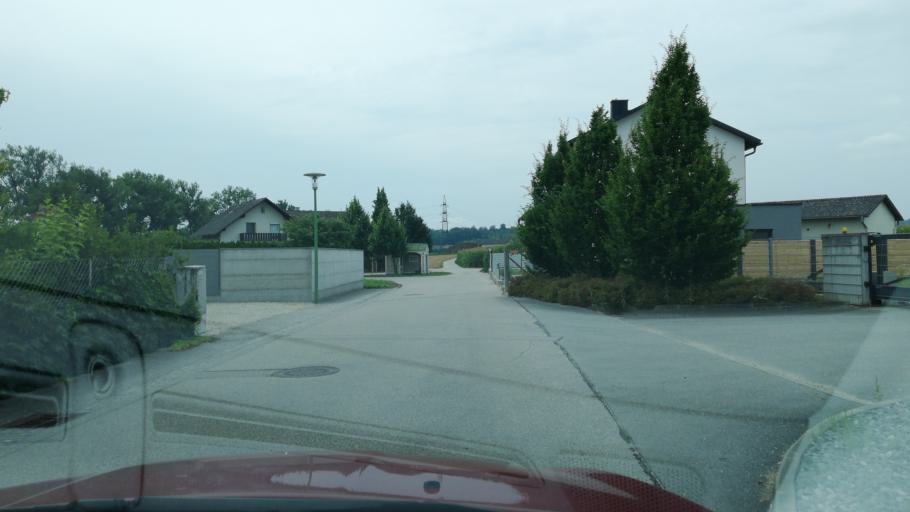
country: AT
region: Upper Austria
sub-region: Politischer Bezirk Urfahr-Umgebung
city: Feldkirchen an der Donau
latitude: 48.3049
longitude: 14.0122
